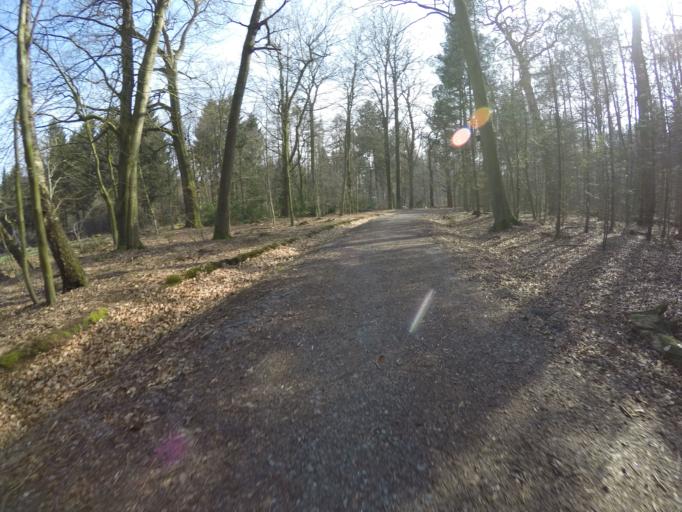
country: DE
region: Schleswig-Holstein
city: Borstel-Hohenraden
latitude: 53.7139
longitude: 9.8001
